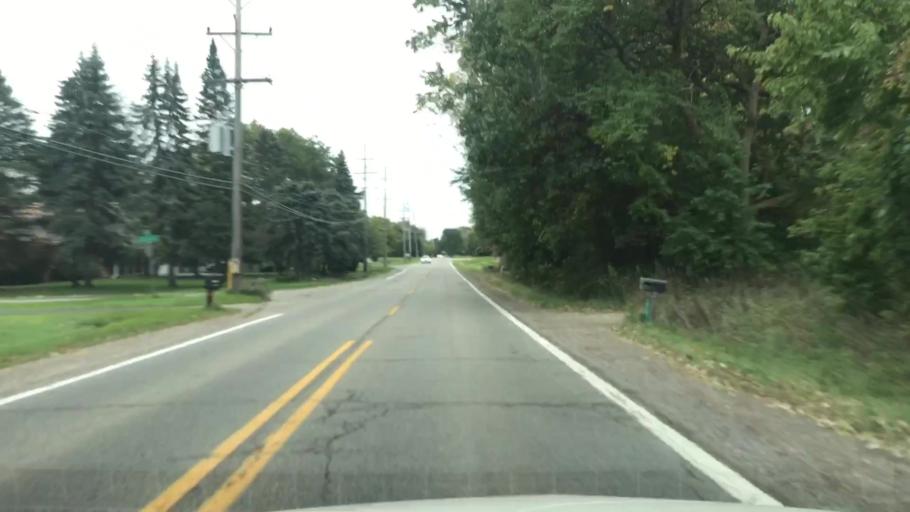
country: US
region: Michigan
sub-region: Macomb County
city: Shelby
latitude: 42.7213
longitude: -83.0562
